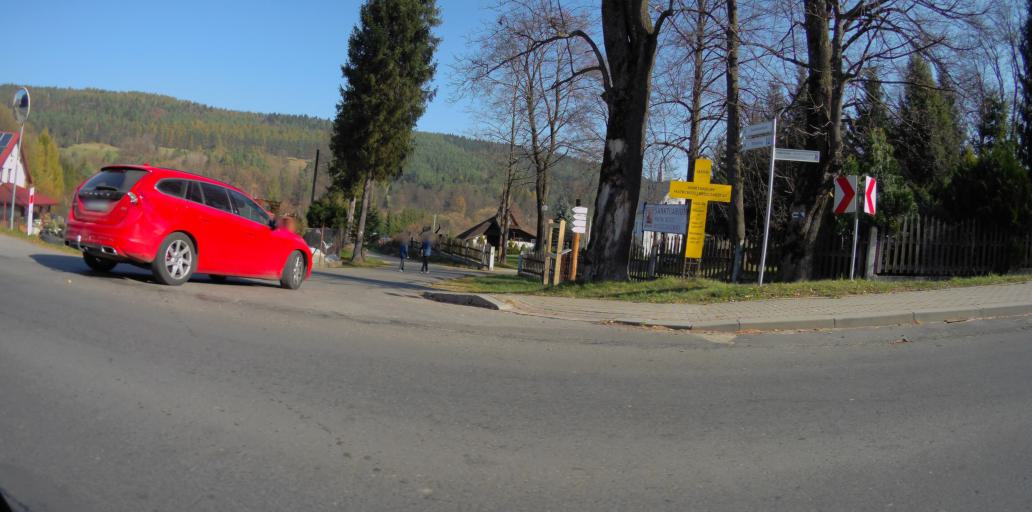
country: PL
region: Subcarpathian Voivodeship
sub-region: Powiat bieszczadzki
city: Ustrzyki Dolne
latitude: 49.4219
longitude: 22.6132
